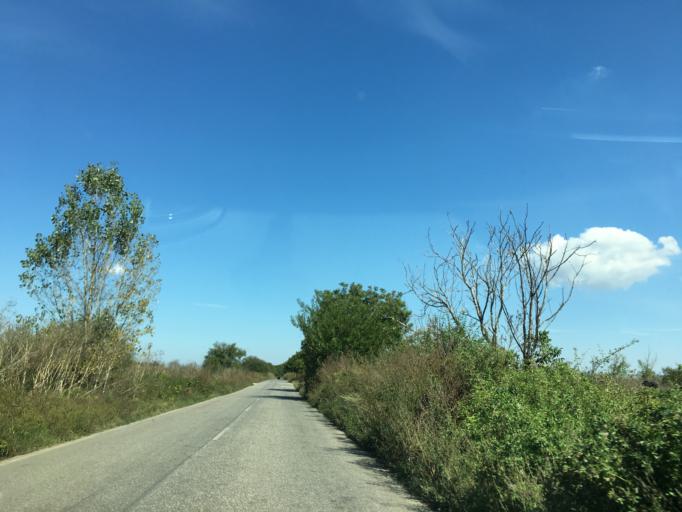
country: RO
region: Olt
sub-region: Comuna Orlea
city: Orlea
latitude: 43.6130
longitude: 24.3670
